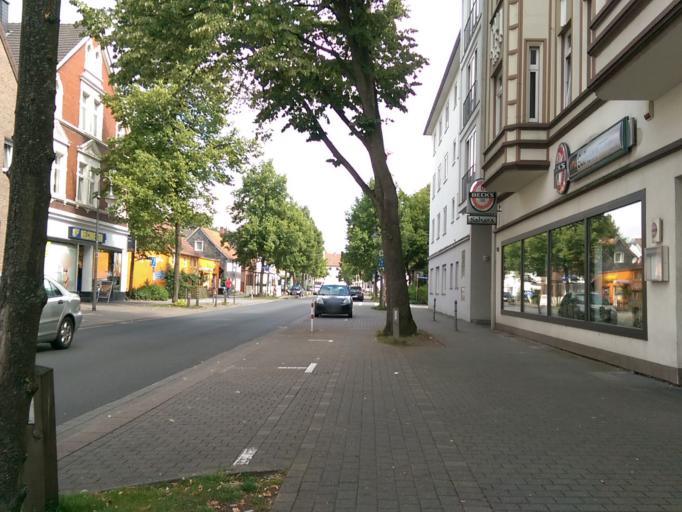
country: DE
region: North Rhine-Westphalia
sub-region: Regierungsbezirk Detmold
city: Guetersloh
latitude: 51.9107
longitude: 8.3837
